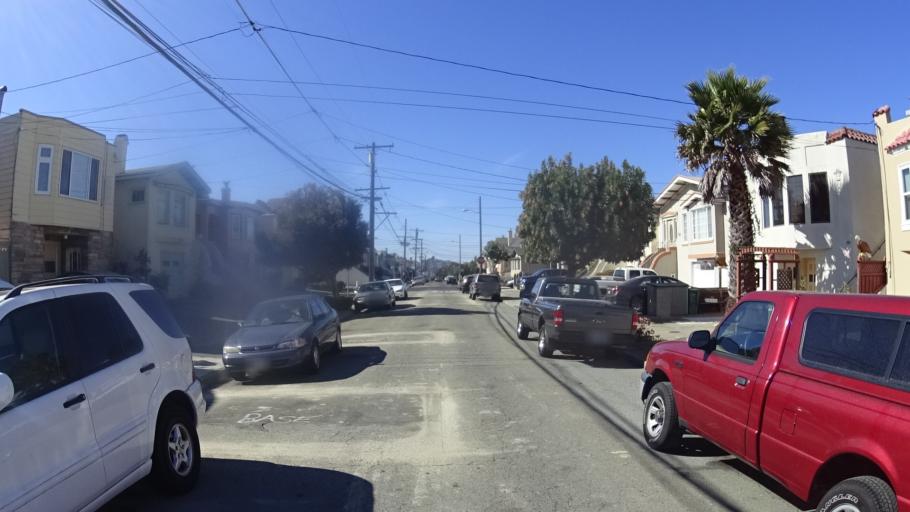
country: US
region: California
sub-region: San Mateo County
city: Daly City
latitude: 37.7118
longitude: -122.4328
